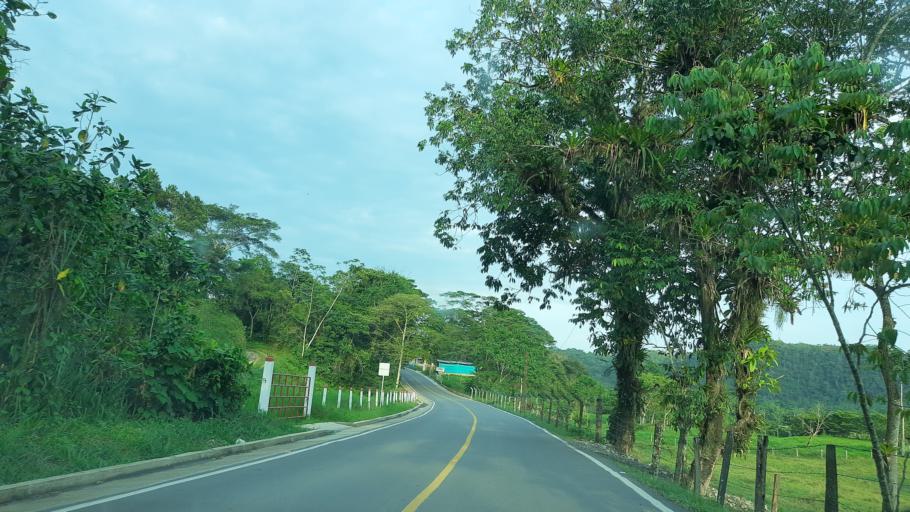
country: CO
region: Boyaca
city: San Luis de Gaceno
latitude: 4.8155
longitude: -73.1779
